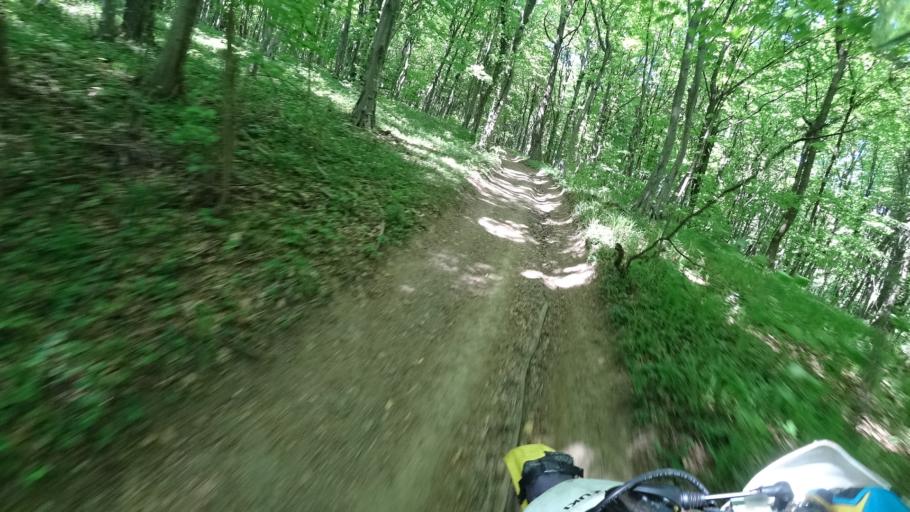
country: HR
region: Zagrebacka
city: Jablanovec
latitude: 45.8605
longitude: 15.8831
